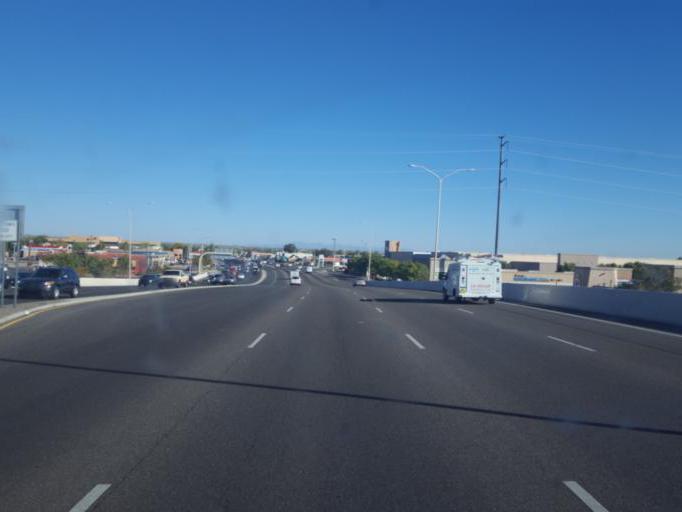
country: US
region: New Mexico
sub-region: Bernalillo County
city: Albuquerque
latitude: 35.1127
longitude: -106.7021
